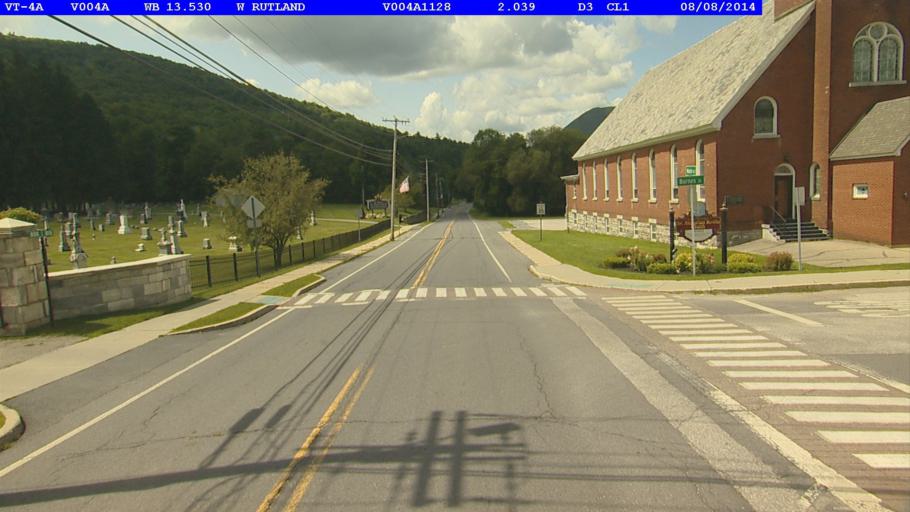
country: US
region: Vermont
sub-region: Rutland County
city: West Rutland
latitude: 43.5968
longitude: -73.0525
